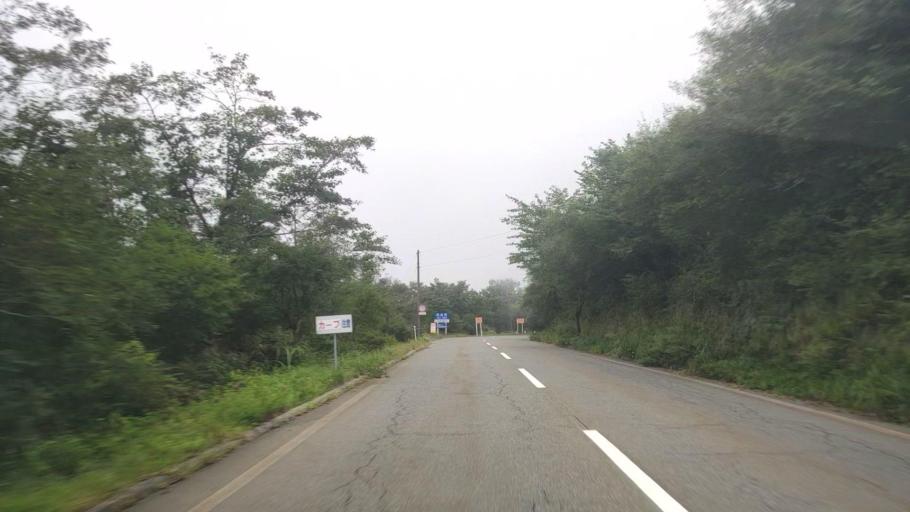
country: JP
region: Shizuoka
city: Gotemba
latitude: 35.3026
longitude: 138.7716
